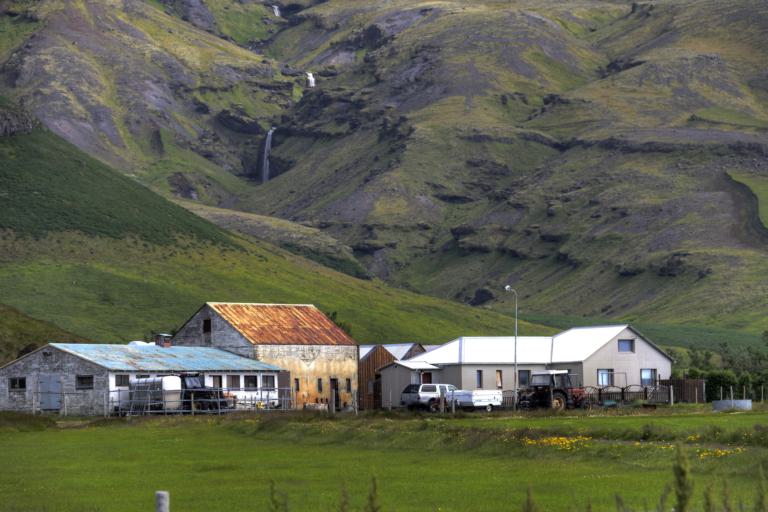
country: IS
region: South
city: Vestmannaeyjar
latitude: 63.5431
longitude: -19.6685
